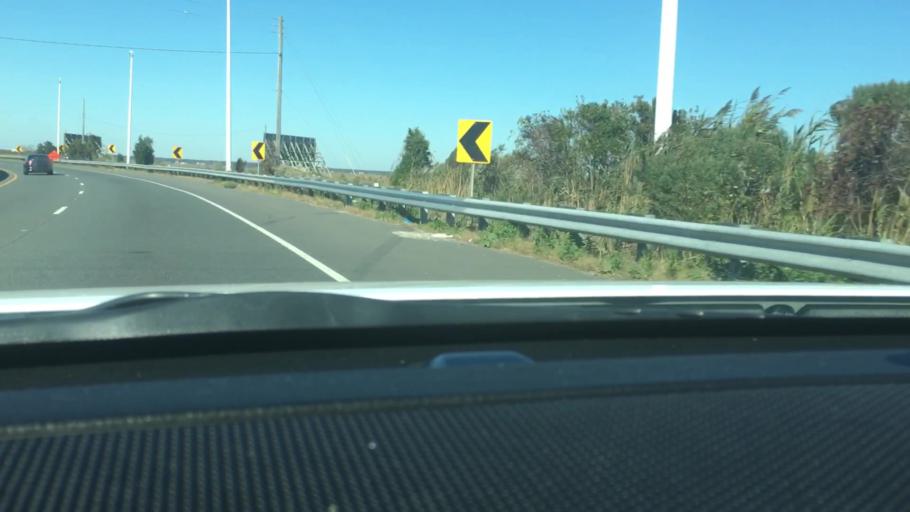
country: US
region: New Jersey
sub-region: Atlantic County
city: Atlantic City
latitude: 39.3841
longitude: -74.4602
